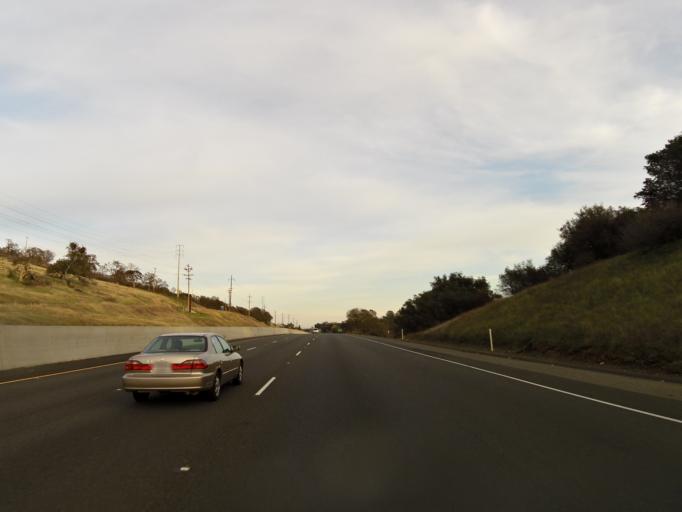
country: US
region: California
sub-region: El Dorado County
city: Cameron Park
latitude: 38.6552
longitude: -121.0248
